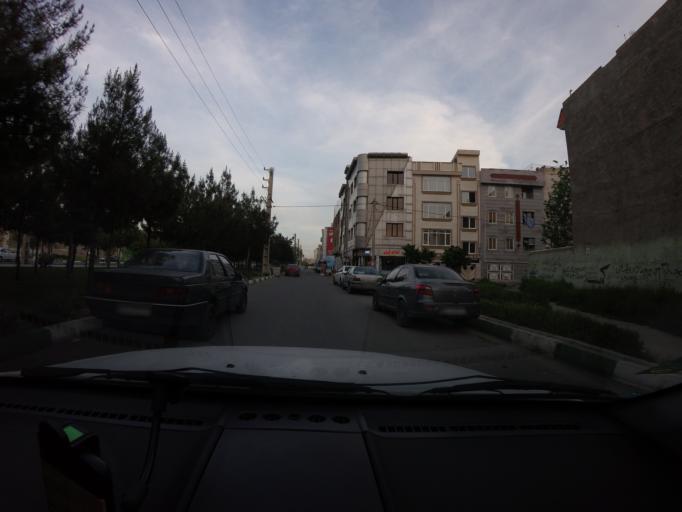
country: IR
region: Tehran
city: Eslamshahr
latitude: 35.5357
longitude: 51.2135
